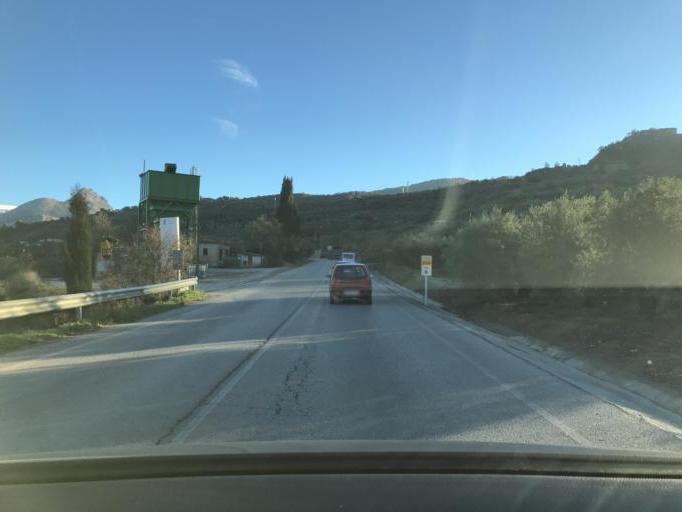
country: ES
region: Andalusia
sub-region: Provincia de Granada
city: Guevejar
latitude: 37.2593
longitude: -3.5924
